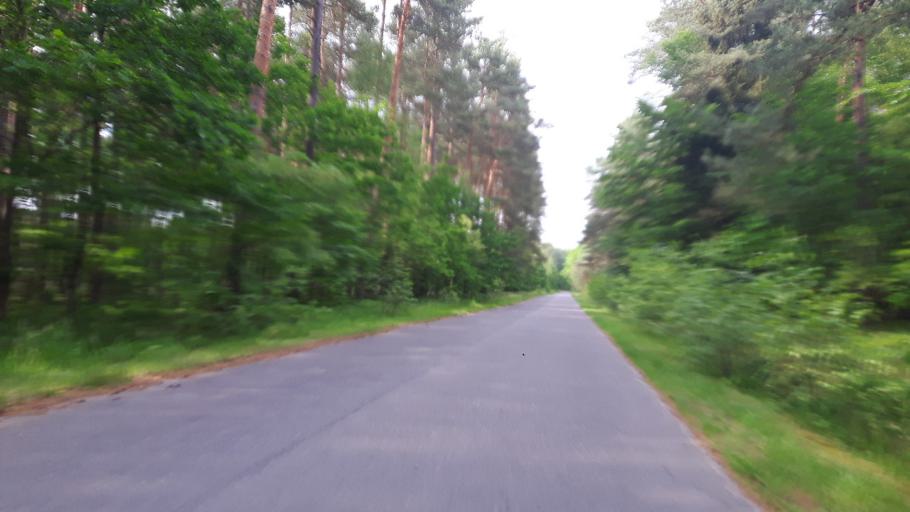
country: PL
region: West Pomeranian Voivodeship
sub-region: Powiat goleniowski
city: Nowogard
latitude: 53.7999
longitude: 15.1276
